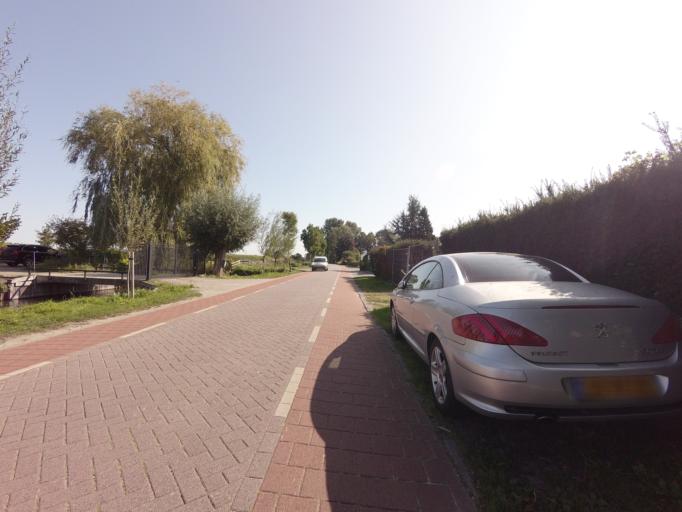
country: NL
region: Utrecht
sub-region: Gemeente Utrecht
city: Utrecht
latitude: 52.1415
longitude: 5.1000
